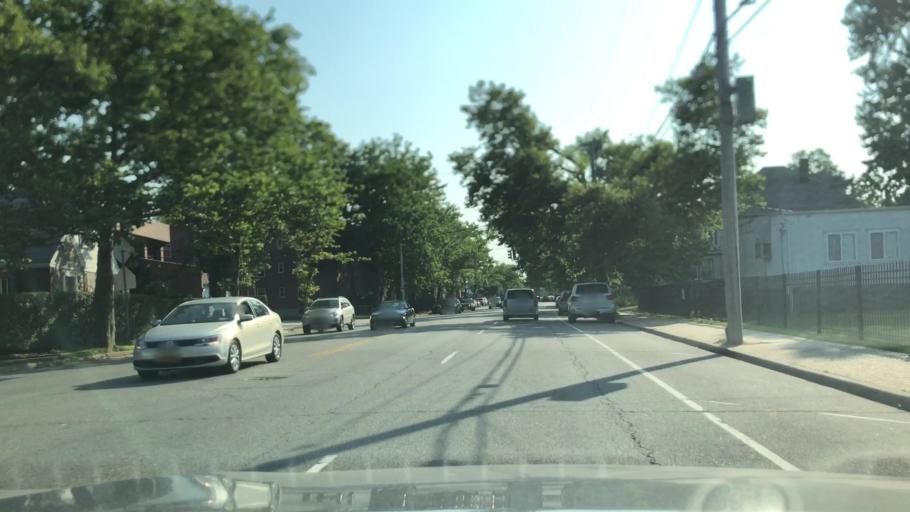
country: US
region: New York
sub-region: Nassau County
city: Hempstead
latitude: 40.7026
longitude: -73.6116
